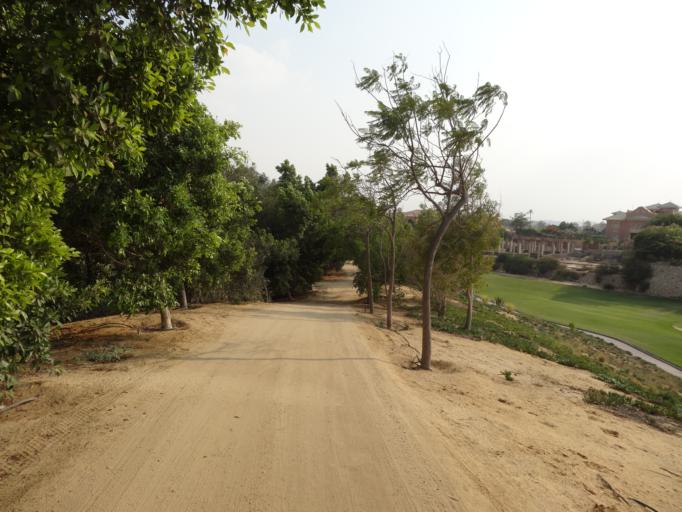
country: EG
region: Muhafazat al Qalyubiyah
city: Al Khankah
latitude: 30.0676
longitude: 31.4343
